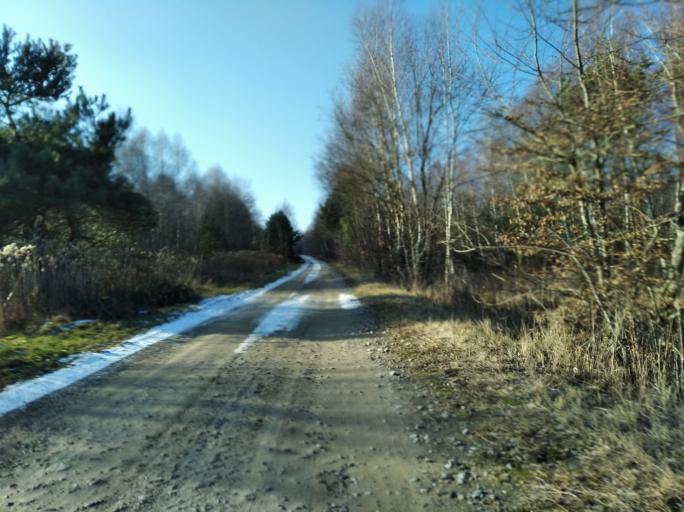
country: PL
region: Subcarpathian Voivodeship
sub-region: Powiat strzyzowski
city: Jawornik
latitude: 49.8307
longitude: 21.8649
